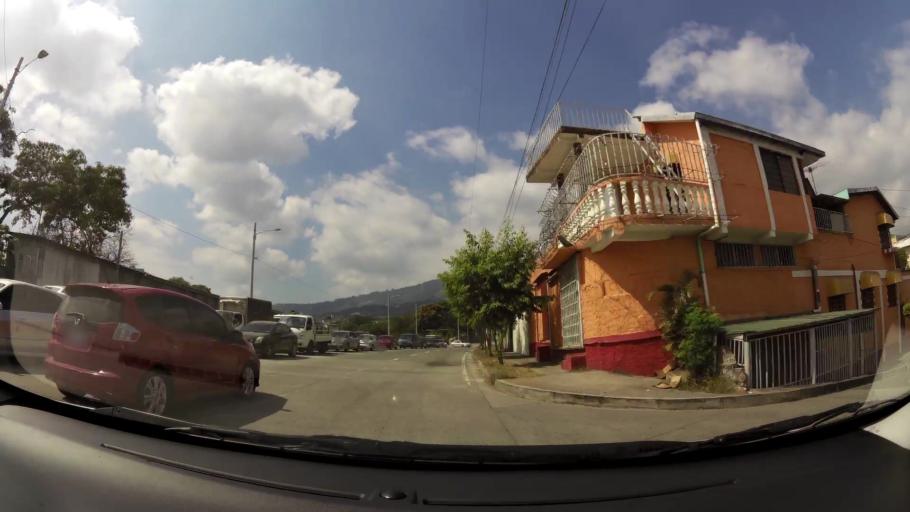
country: SV
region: San Salvador
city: Mejicanos
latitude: 13.7108
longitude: -89.2353
